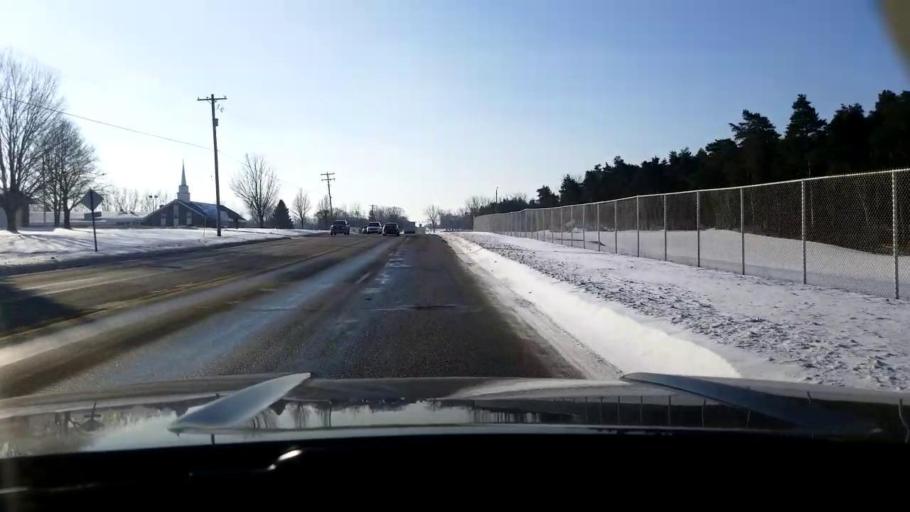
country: US
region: Michigan
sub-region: Jackson County
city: Jackson
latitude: 42.2825
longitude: -84.3844
